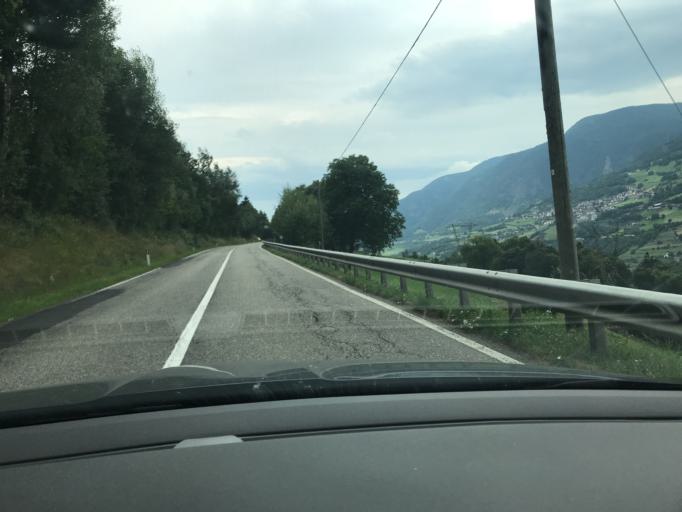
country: IT
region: Trentino-Alto Adige
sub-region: Bolzano
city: Villandro
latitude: 46.6169
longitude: 11.5474
